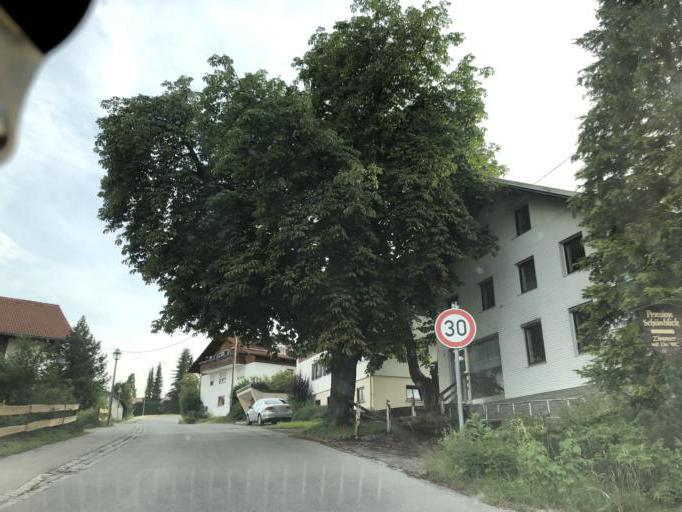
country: DE
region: Bavaria
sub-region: Swabia
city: Oy-Mittelberg
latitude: 47.6444
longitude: 10.4519
